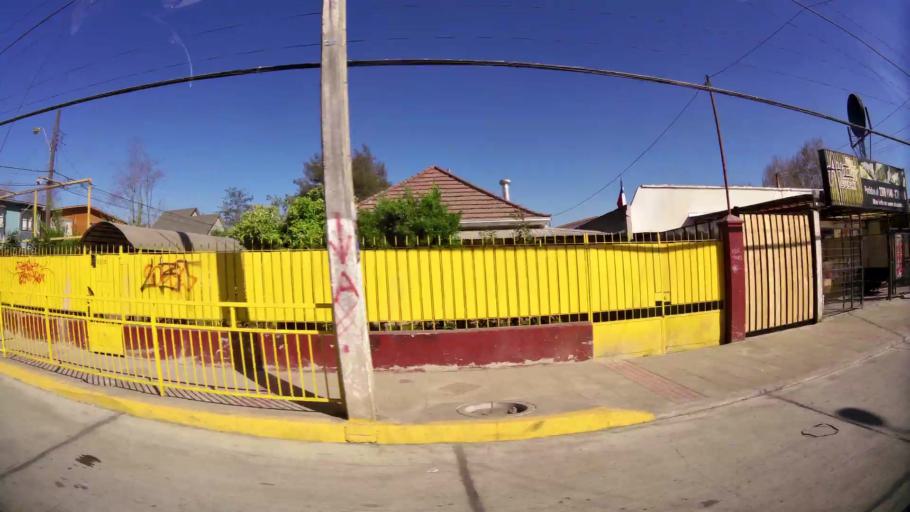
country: CL
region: Santiago Metropolitan
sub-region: Provincia de Talagante
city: Penaflor
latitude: -33.6070
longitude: -70.8971
